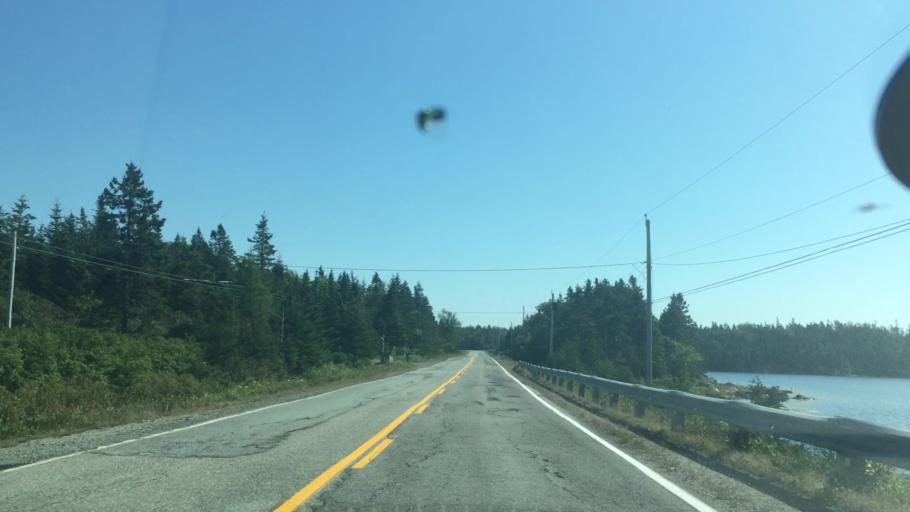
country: CA
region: Nova Scotia
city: New Glasgow
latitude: 44.9035
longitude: -62.4090
